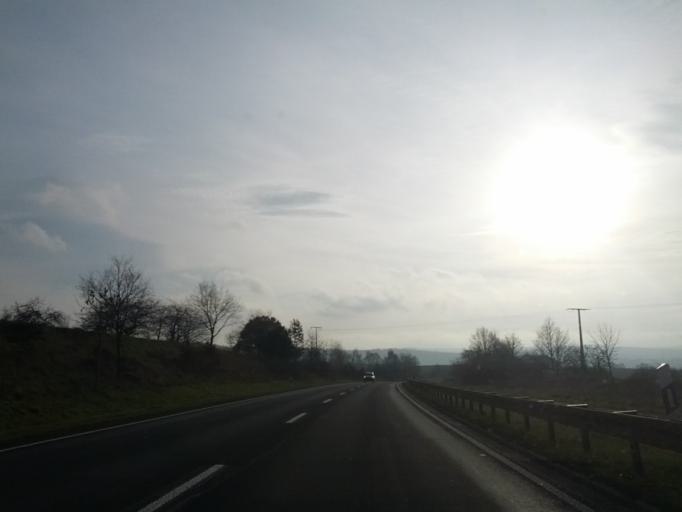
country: DE
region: Thuringia
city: Breitungen
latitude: 50.7585
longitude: 10.3523
